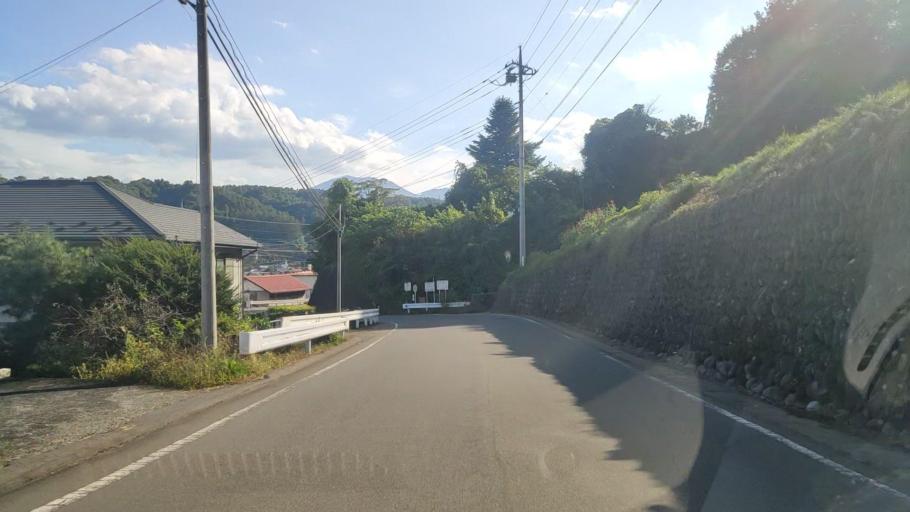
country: JP
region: Nagano
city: Komoro
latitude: 36.5369
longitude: 138.5498
